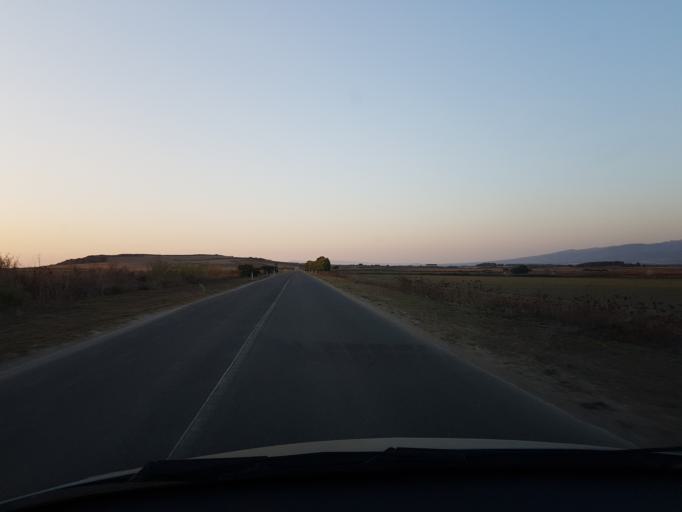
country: IT
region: Sardinia
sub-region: Provincia di Oristano
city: Nurachi
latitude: 39.9694
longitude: 8.4528
